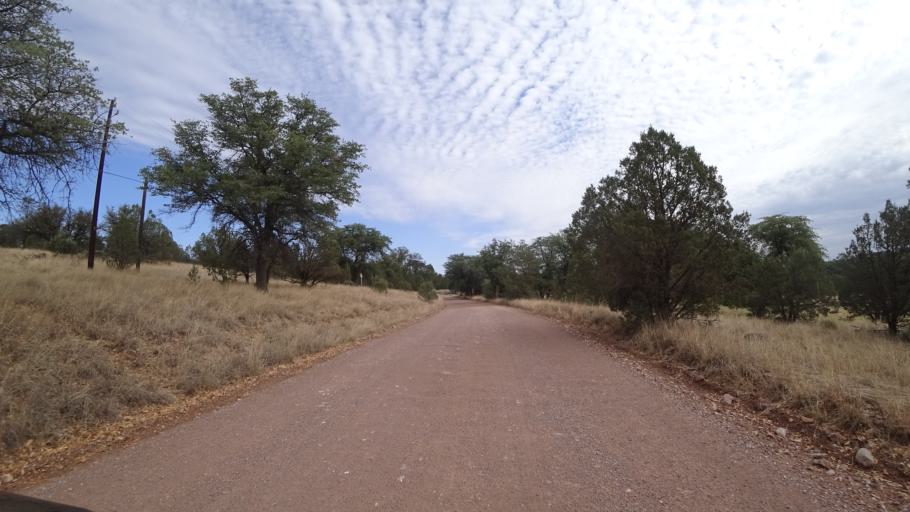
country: US
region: Arizona
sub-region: Cochise County
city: Huachuca City
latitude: 31.5356
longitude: -110.5292
